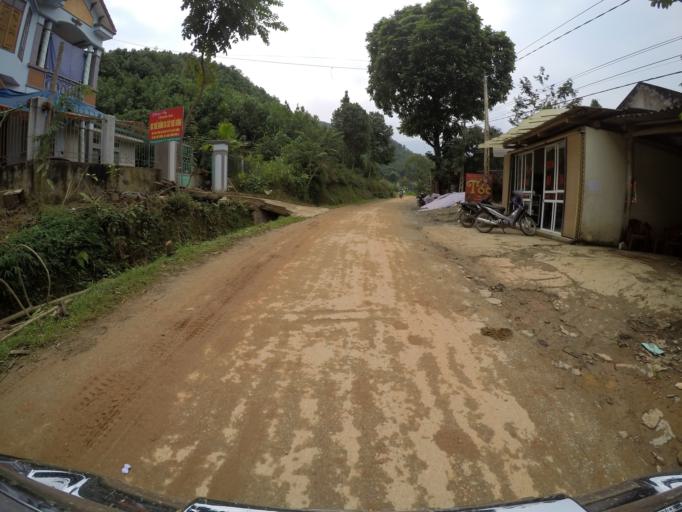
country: VN
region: Yen Bai
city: Co Phuc
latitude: 21.8424
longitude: 104.6167
